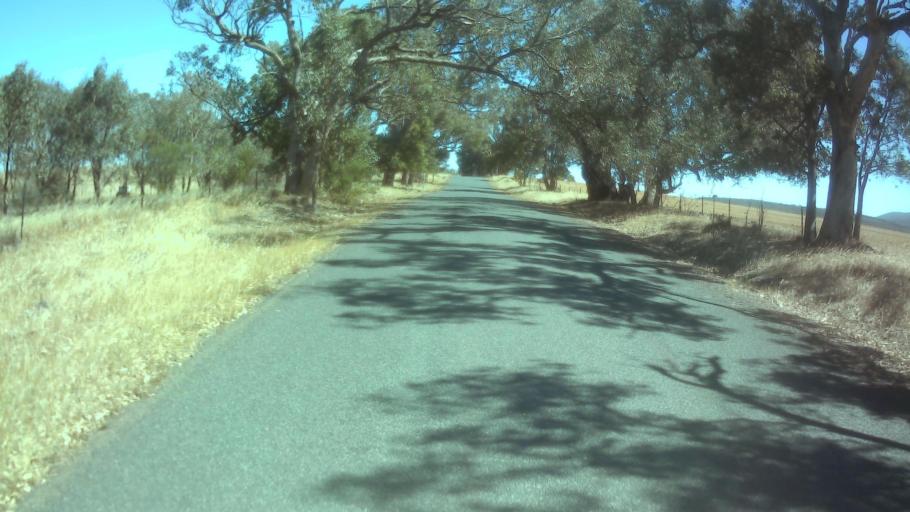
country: AU
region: New South Wales
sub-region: Weddin
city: Grenfell
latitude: -33.9443
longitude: 148.3881
